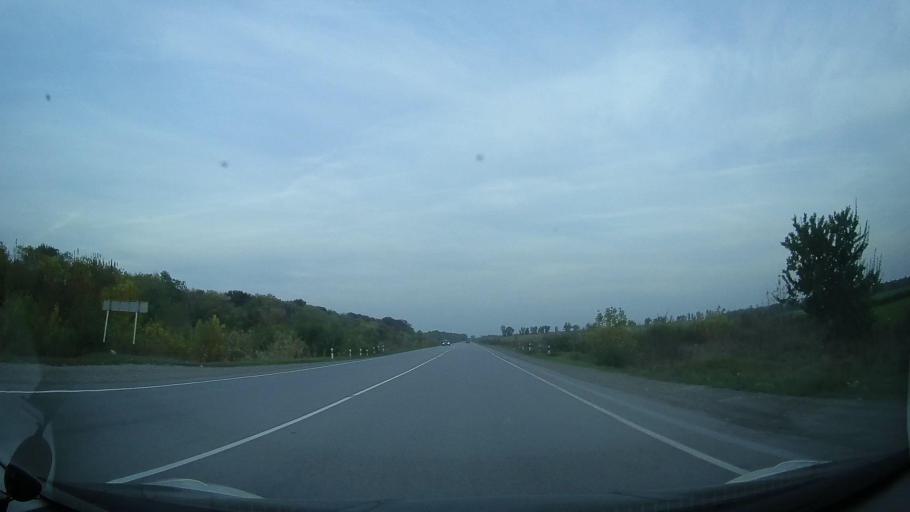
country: RU
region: Rostov
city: Ol'ginskaya
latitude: 47.1307
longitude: 39.9303
